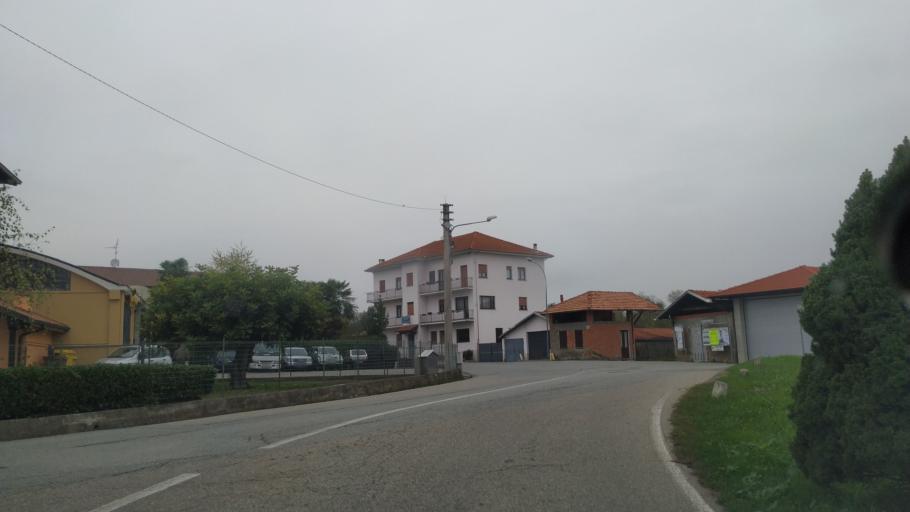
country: IT
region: Piedmont
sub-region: Provincia di Biella
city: Lessona
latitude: 45.5768
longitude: 8.2027
